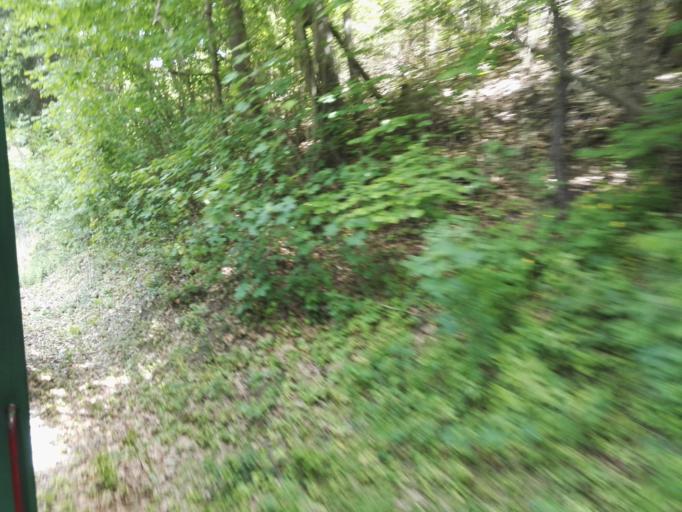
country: AT
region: Styria
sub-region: Politischer Bezirk Weiz
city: Anger
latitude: 47.2848
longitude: 15.6915
